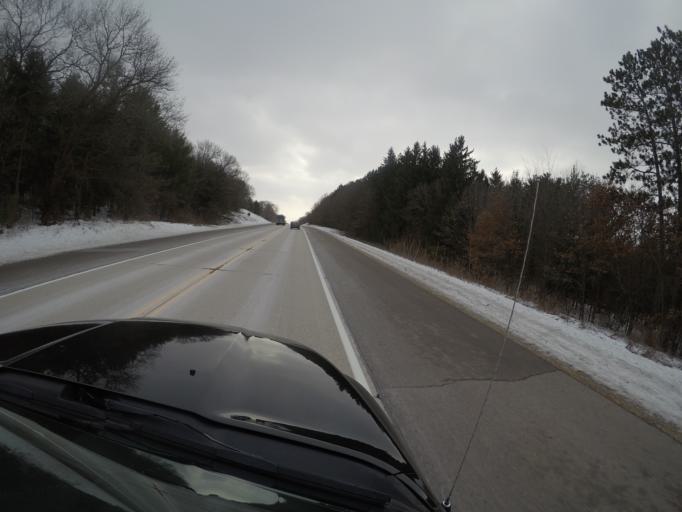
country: US
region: Wisconsin
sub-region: Trempealeau County
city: Galesville
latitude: 44.0556
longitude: -91.2912
